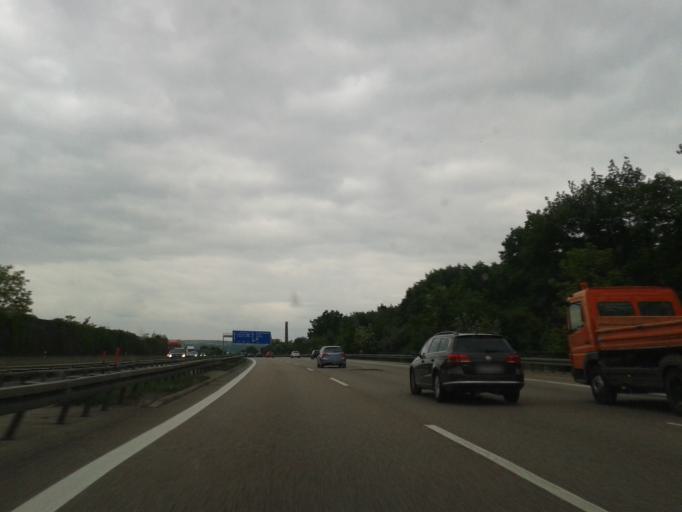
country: DE
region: Saxony
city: Radebeul
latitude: 51.0966
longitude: 13.6999
